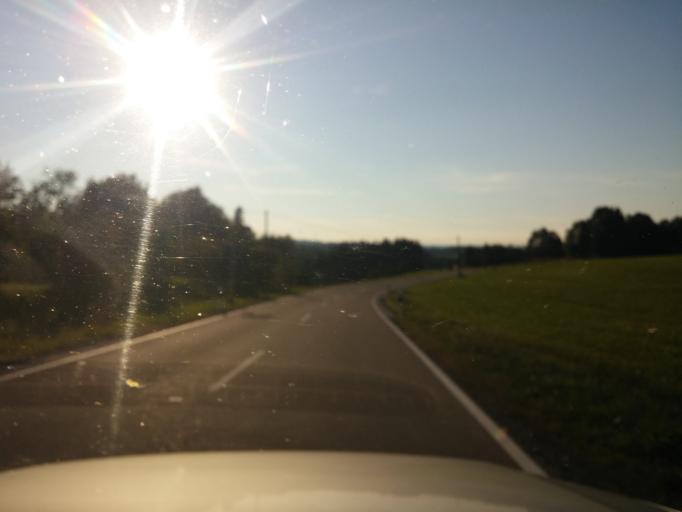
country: DE
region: Bavaria
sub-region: Swabia
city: Wiggensbach
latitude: 47.7682
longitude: 10.2144
